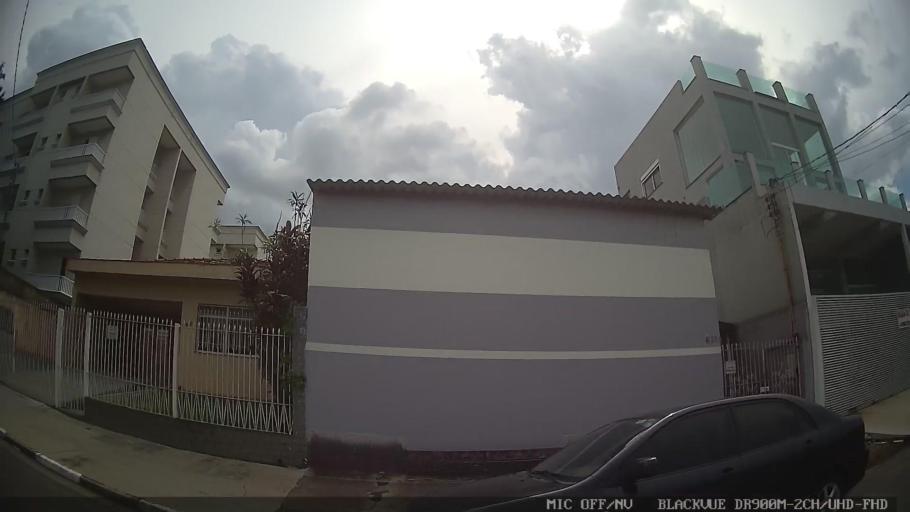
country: BR
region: Sao Paulo
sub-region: Atibaia
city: Atibaia
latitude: -23.1220
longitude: -46.5644
